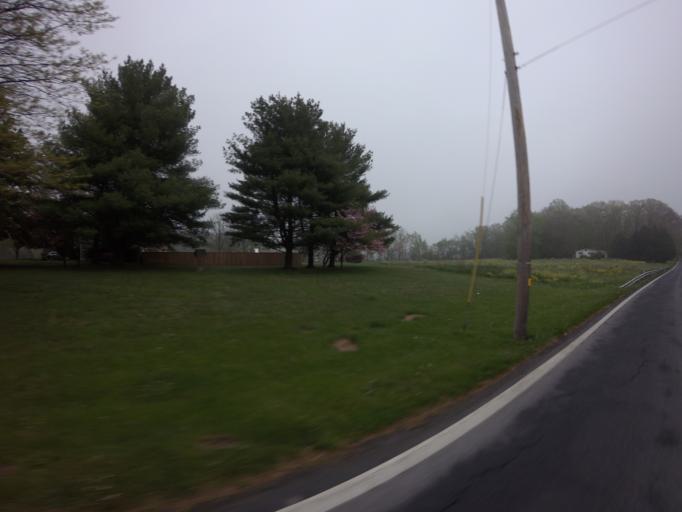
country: US
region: Maryland
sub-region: Carroll County
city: Eldersburg
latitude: 39.4867
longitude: -76.9591
